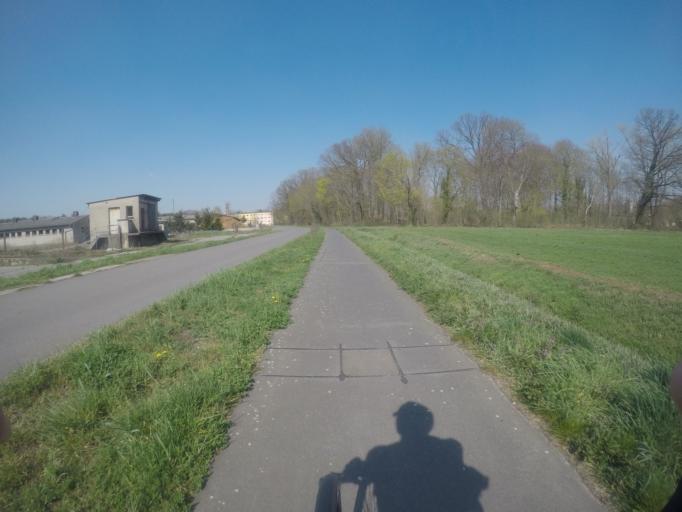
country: DE
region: Brandenburg
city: Falkensee
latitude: 52.6361
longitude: 13.0855
